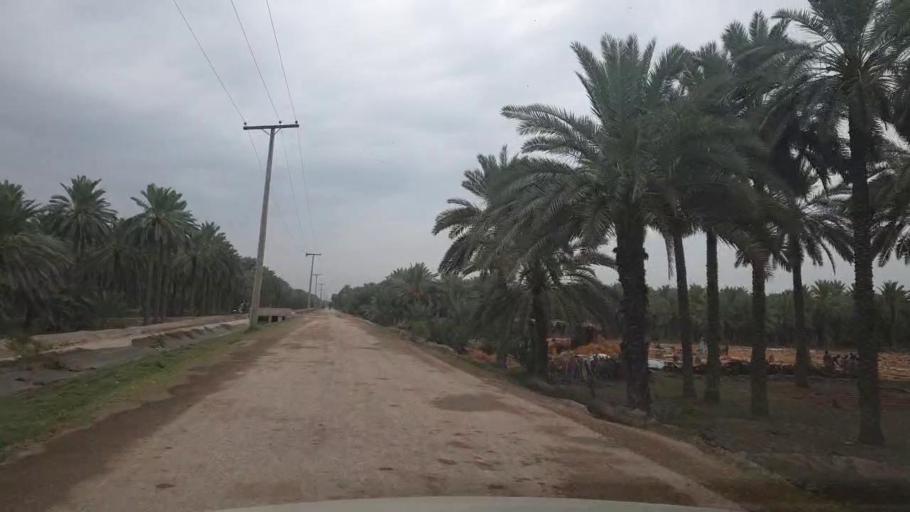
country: PK
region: Sindh
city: Khairpur
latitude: 27.6118
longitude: 68.8175
